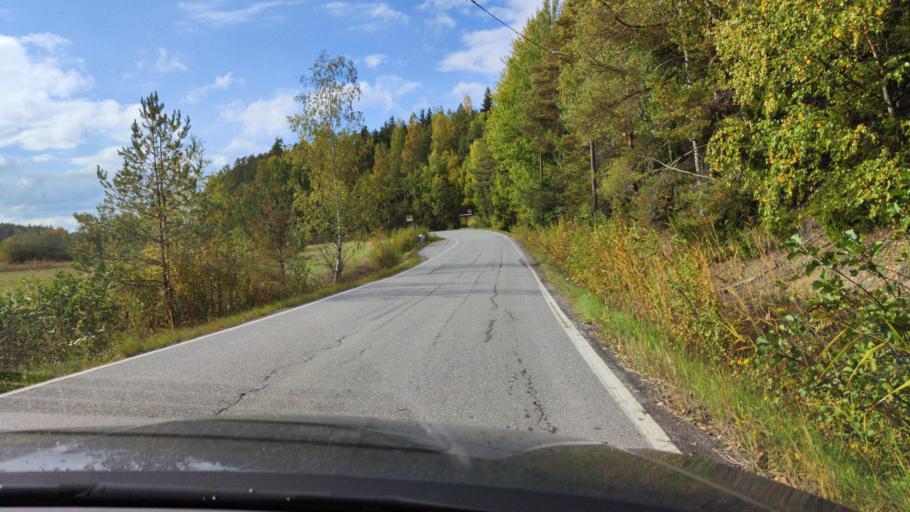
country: FI
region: Varsinais-Suomi
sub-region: Aboland-Turunmaa
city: Pargas
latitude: 60.3473
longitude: 22.2046
